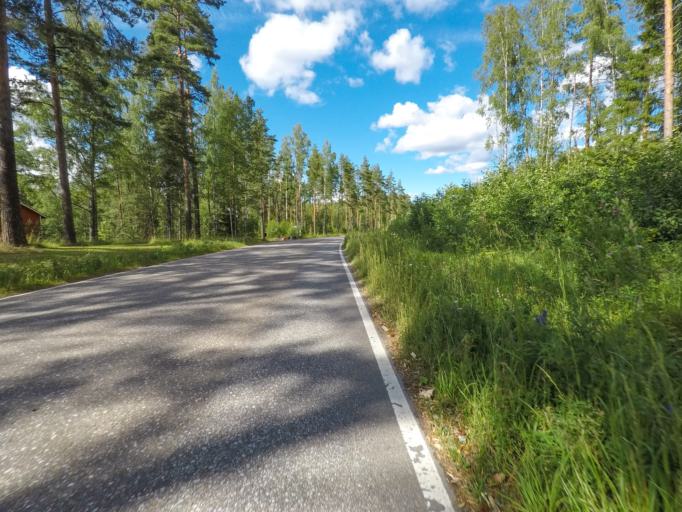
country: FI
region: South Karelia
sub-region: Lappeenranta
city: Joutseno
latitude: 61.1049
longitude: 28.3713
